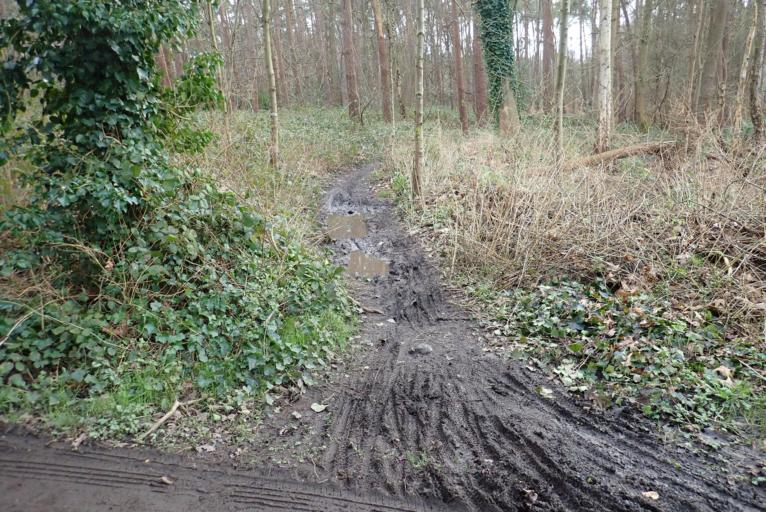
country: BE
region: Flanders
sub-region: Provincie Oost-Vlaanderen
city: Temse
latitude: 51.1783
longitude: 4.2040
